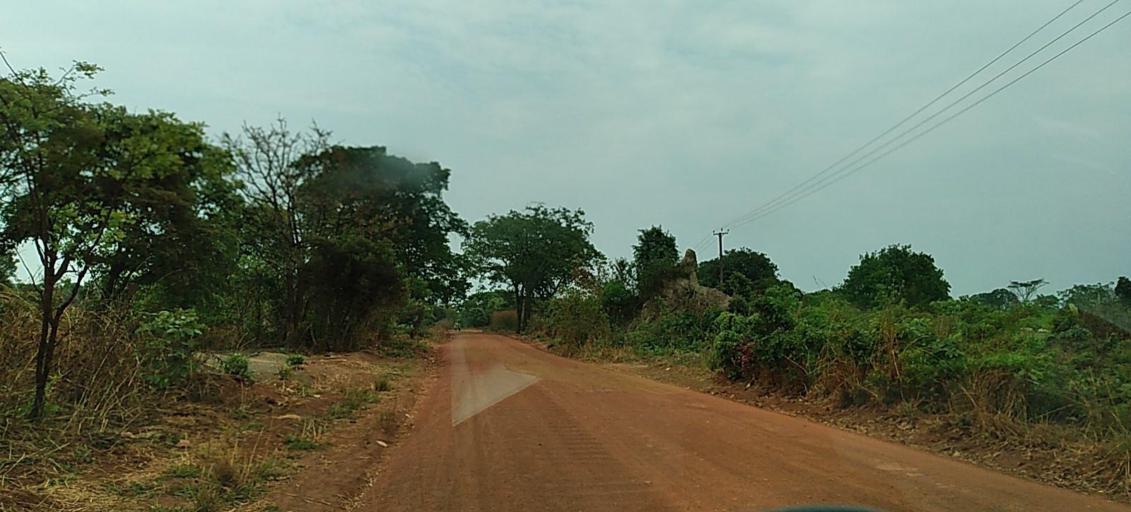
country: ZM
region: North-Western
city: Solwezi
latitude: -12.2388
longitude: 26.5114
